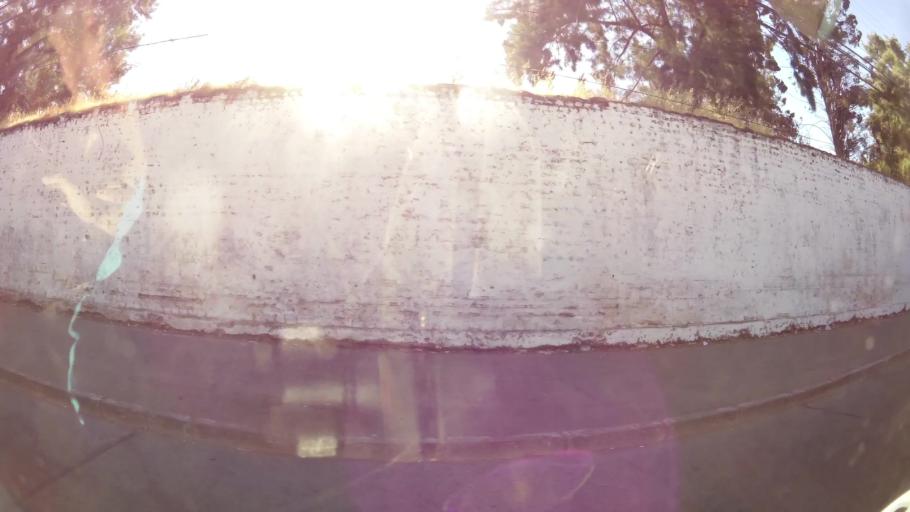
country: CL
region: O'Higgins
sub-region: Provincia de Colchagua
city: Chimbarongo
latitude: -34.5784
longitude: -70.9942
